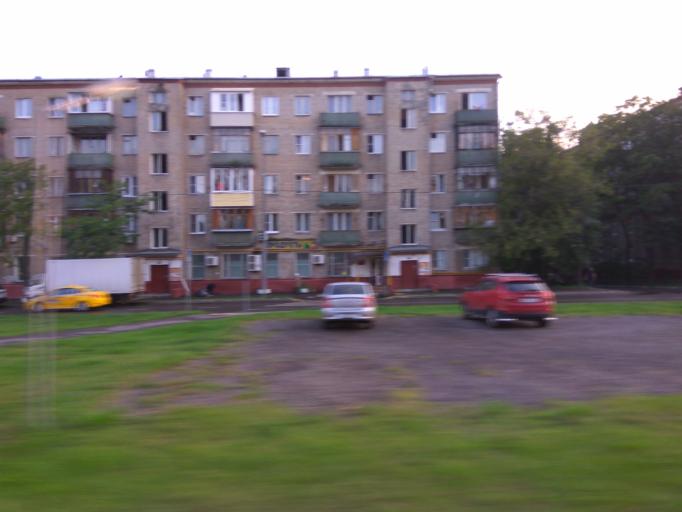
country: RU
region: Moskovskaya
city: Bogorodskoye
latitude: 55.8162
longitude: 37.7292
